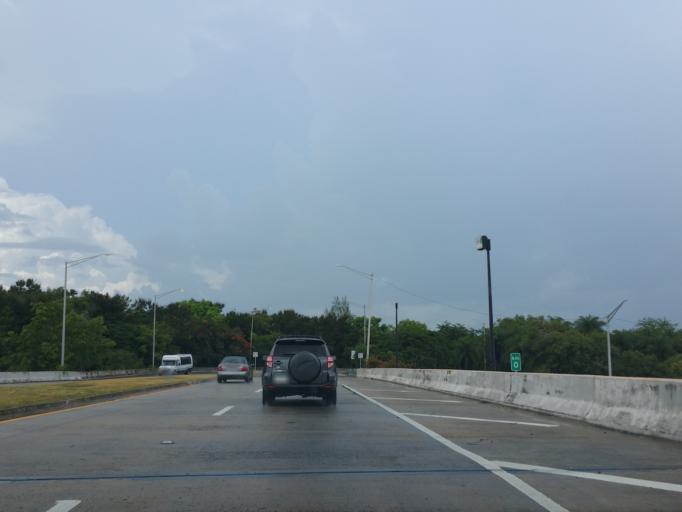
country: PR
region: Trujillo Alto
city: Trujillo Alto
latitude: 18.4383
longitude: -66.0223
